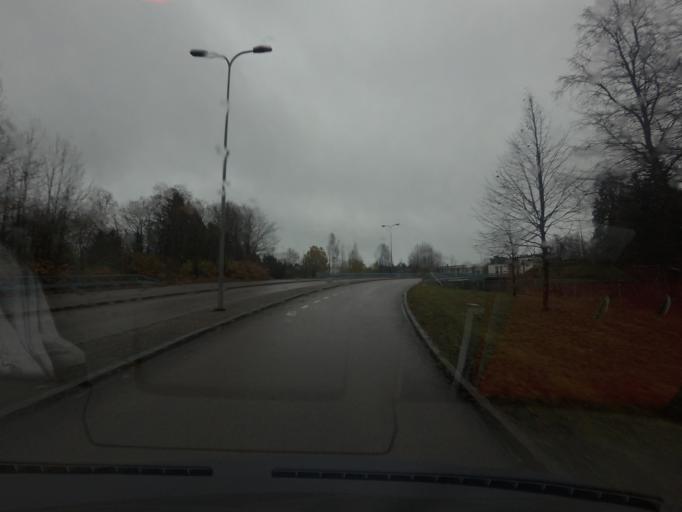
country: FI
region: Uusimaa
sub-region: Helsinki
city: Espoo
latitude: 60.2081
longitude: 24.6723
